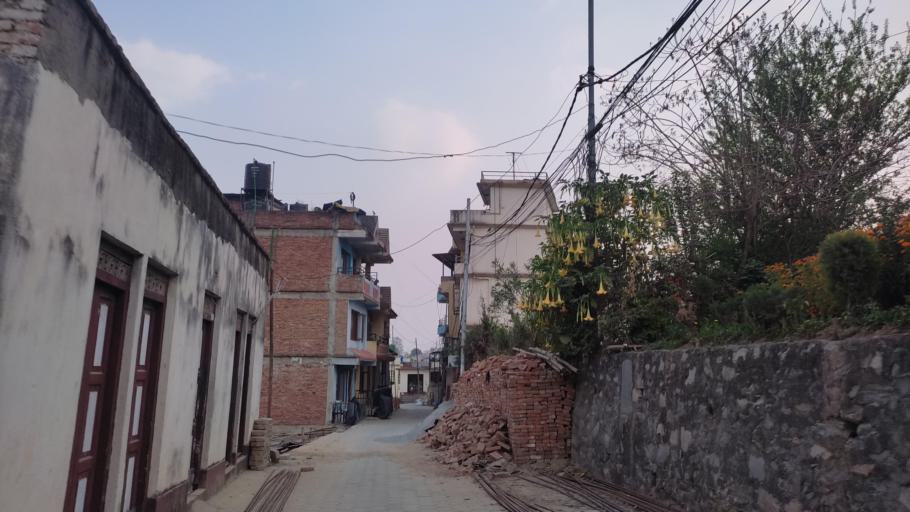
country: NP
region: Central Region
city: Kirtipur
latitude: 27.6706
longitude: 85.2857
